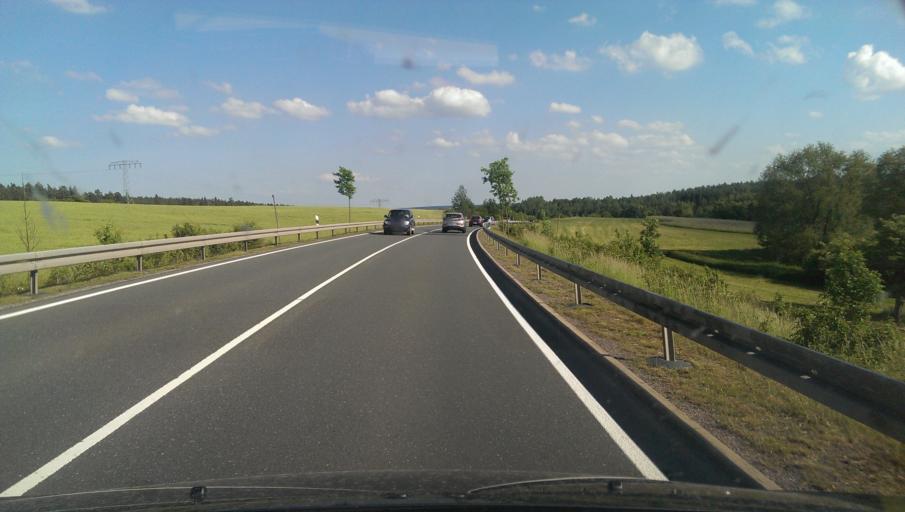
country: DE
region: Thuringia
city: Lederhose
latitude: 50.8028
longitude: 11.9246
